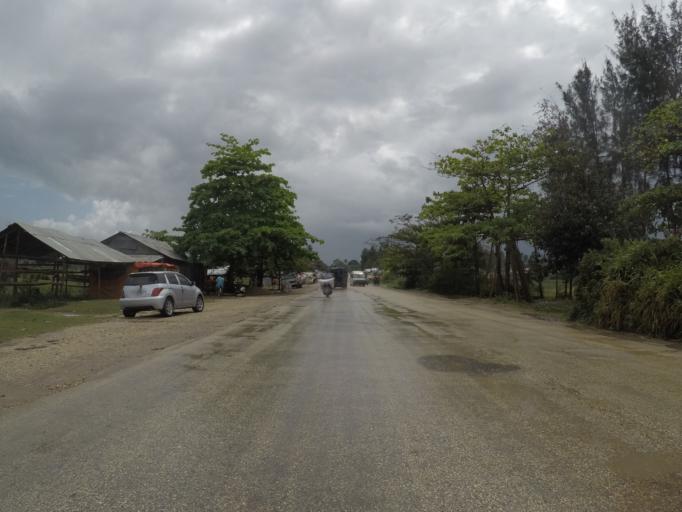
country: TZ
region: Zanzibar Central/South
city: Koani
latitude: -6.0760
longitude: 39.2229
